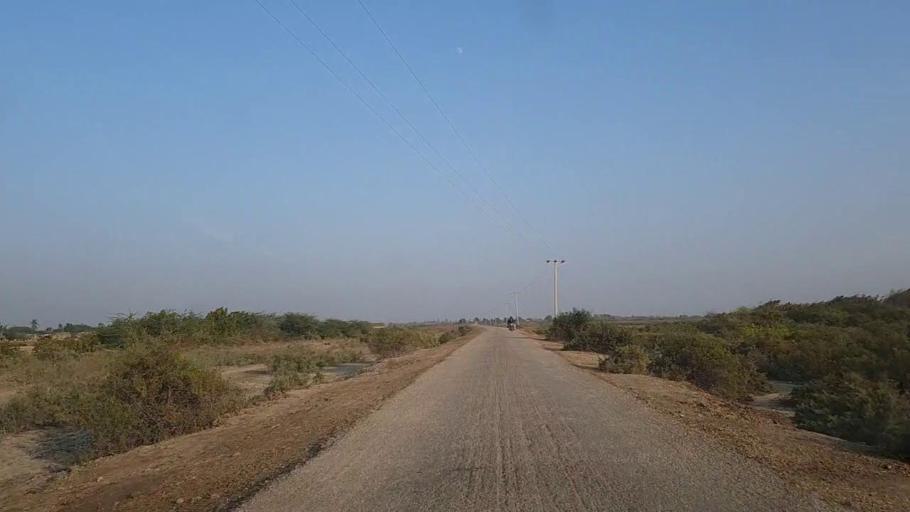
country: PK
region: Sindh
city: Keti Bandar
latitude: 24.2798
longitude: 67.6297
